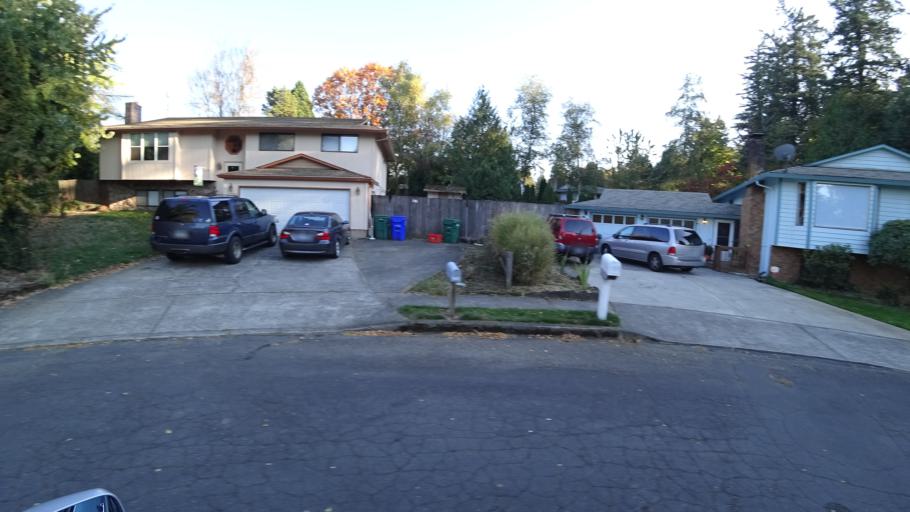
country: US
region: Oregon
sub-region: Multnomah County
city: Gresham
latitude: 45.4841
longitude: -122.4512
